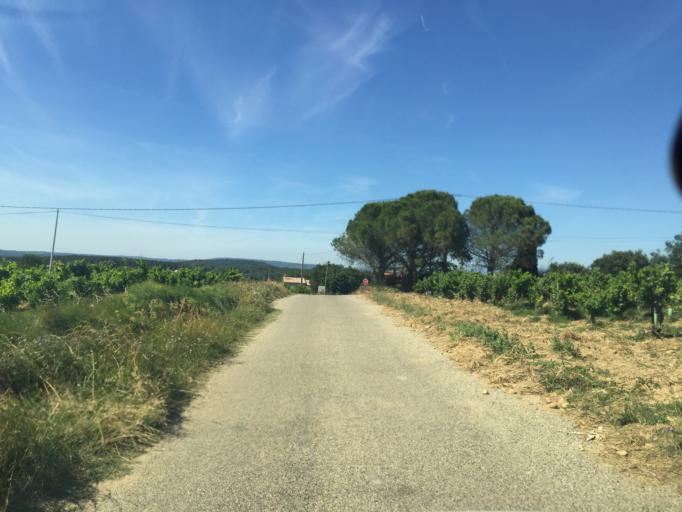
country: FR
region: Provence-Alpes-Cote d'Azur
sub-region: Departement du Vaucluse
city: Chateauneuf-du-Pape
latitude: 44.0913
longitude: 4.8052
